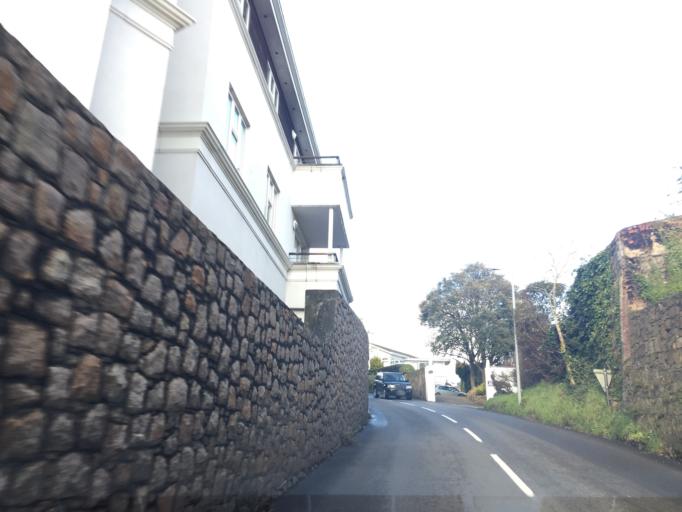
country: JE
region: St Helier
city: Saint Helier
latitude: 49.1991
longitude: -2.1379
